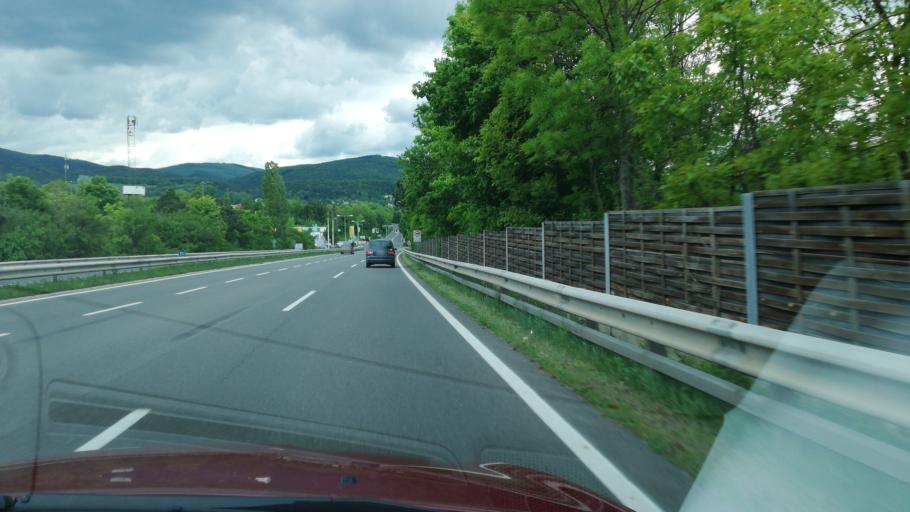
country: AT
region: Lower Austria
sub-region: Politischer Bezirk Baden
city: Baden
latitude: 47.9954
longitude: 16.2301
